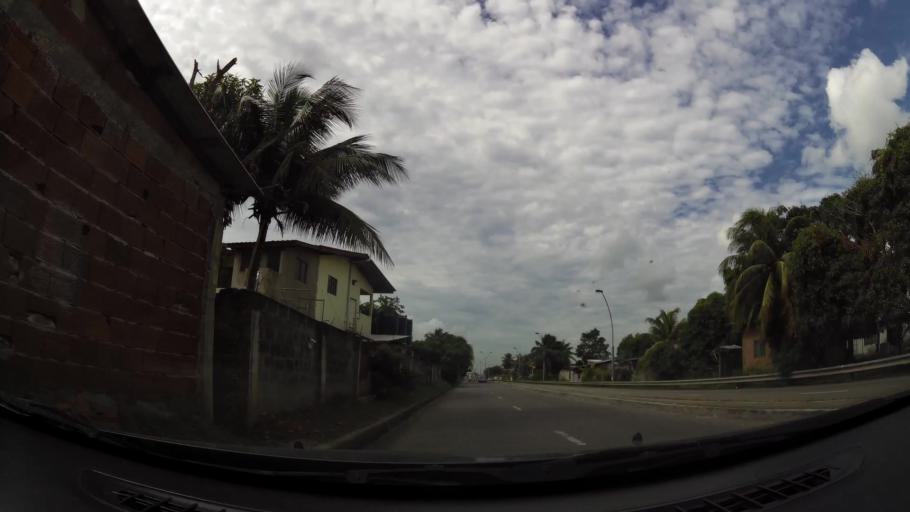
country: TT
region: Chaguanas
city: Chaguanas
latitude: 10.5089
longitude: -61.4006
